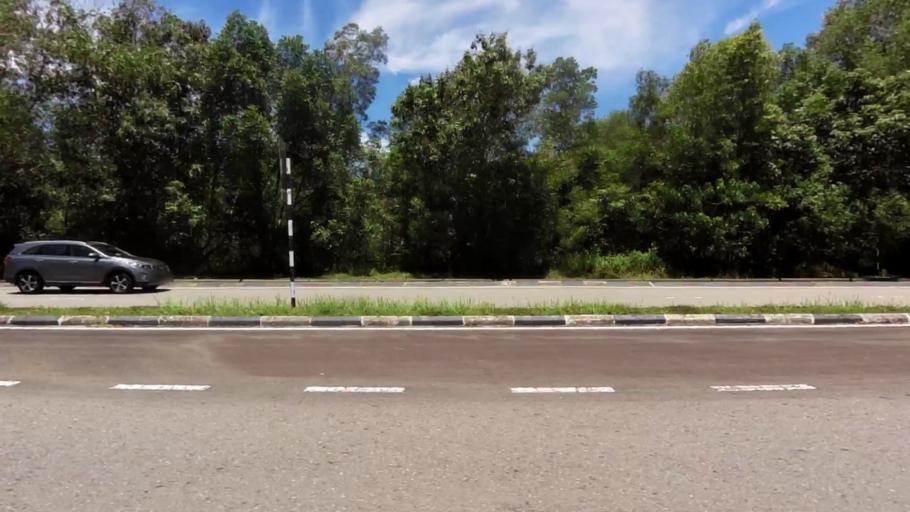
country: BN
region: Brunei and Muara
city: Bandar Seri Begawan
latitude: 4.9169
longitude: 114.9431
